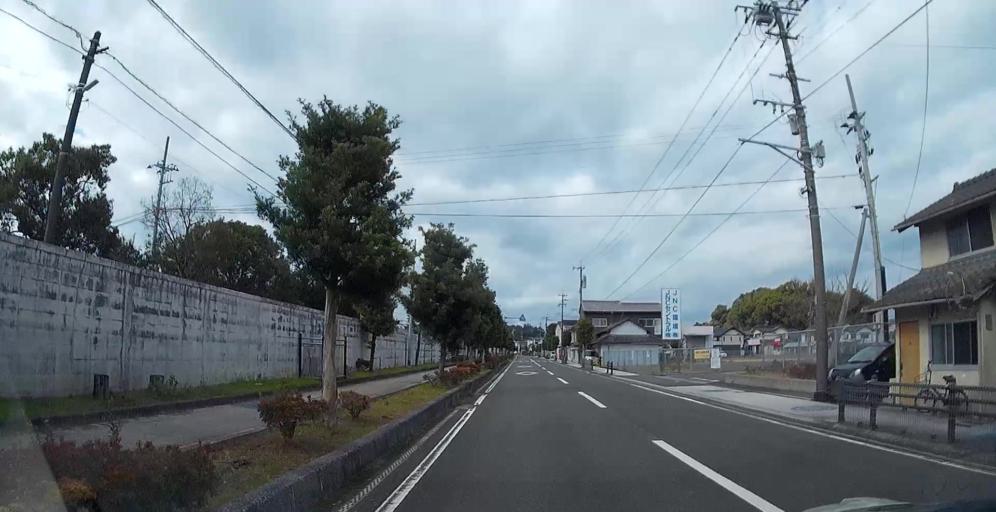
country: JP
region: Kumamoto
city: Minamata
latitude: 32.2112
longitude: 130.3927
